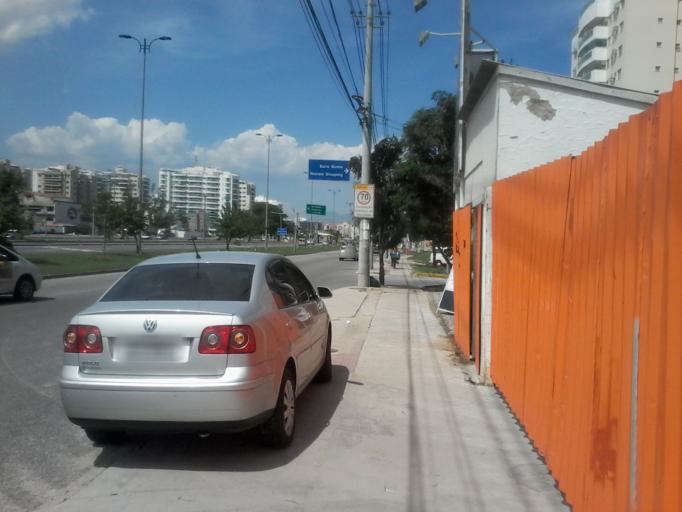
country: BR
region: Rio de Janeiro
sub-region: Nilopolis
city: Nilopolis
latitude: -23.0196
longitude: -43.4858
